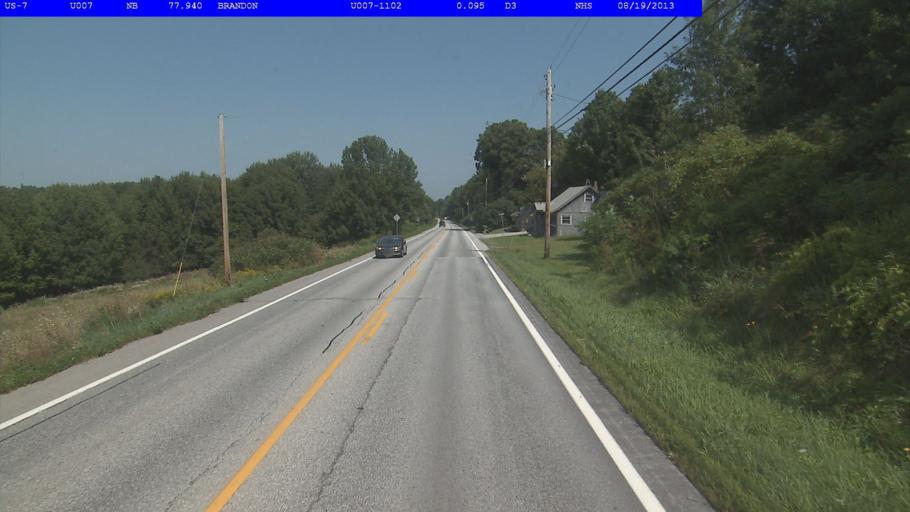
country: US
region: Vermont
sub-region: Rutland County
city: Brandon
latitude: 43.7557
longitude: -73.0484
